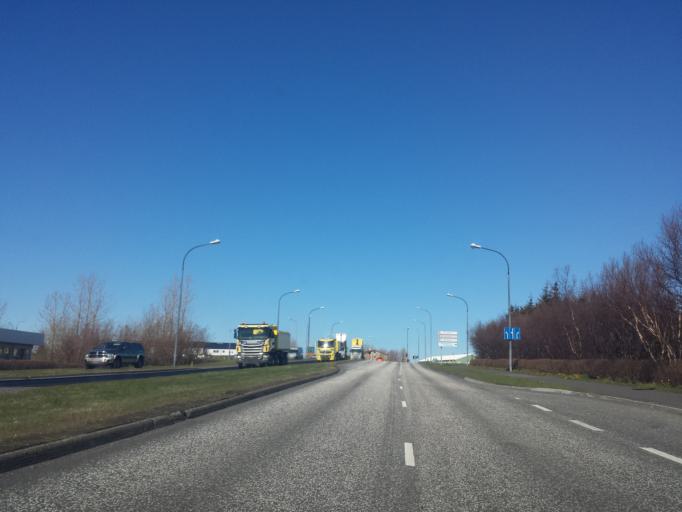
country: IS
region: Capital Region
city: Reykjavik
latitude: 64.1206
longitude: -21.8087
